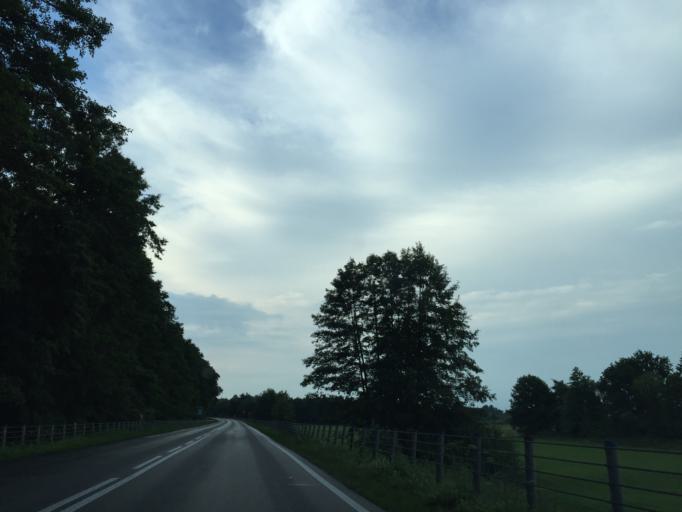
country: PL
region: Masovian Voivodeship
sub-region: Powiat ostrowski
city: Brok
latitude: 52.6870
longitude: 21.8520
